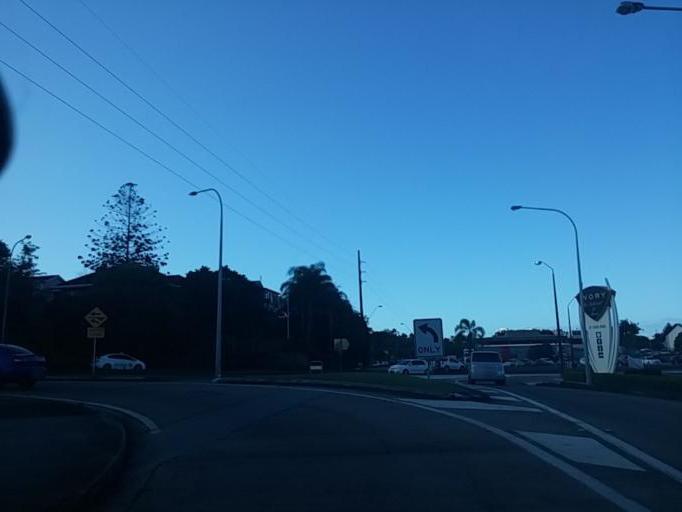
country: AU
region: New South Wales
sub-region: Tweed
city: Tweed Heads West
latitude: -28.1819
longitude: 153.5380
